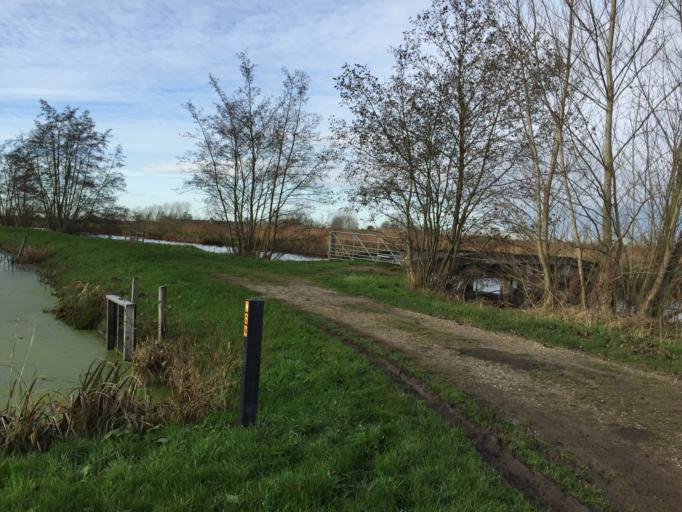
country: NL
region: Utrecht
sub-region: Gemeente Oudewater
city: Oudewater
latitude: 52.0060
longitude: 4.8964
